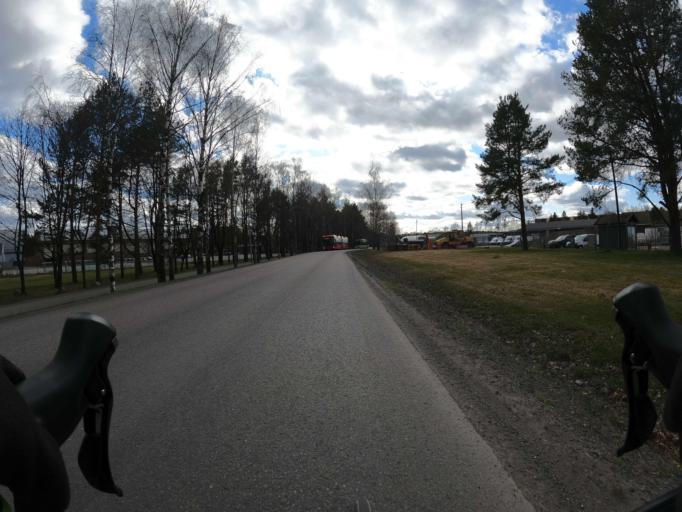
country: NO
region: Akershus
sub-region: Skedsmo
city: Lillestrom
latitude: 59.9635
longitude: 11.0699
